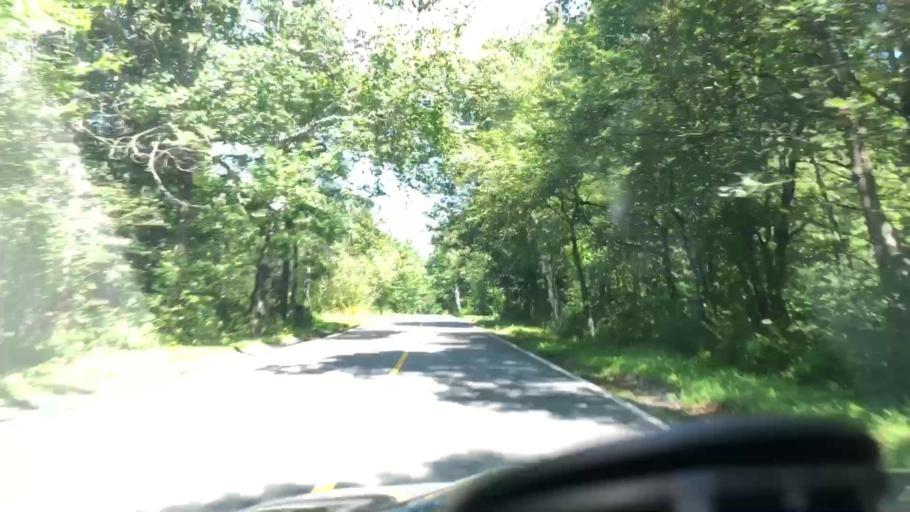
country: US
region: Massachusetts
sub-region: Berkshire County
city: Lanesborough
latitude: 42.5817
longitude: -73.2023
